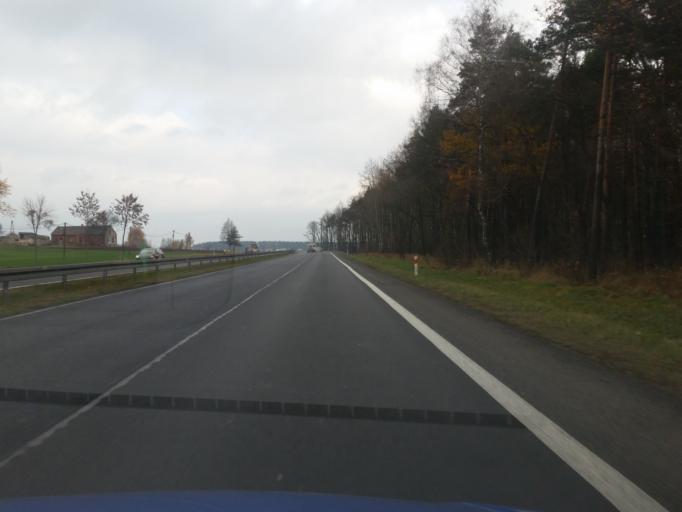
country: PL
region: Silesian Voivodeship
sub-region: Powiat myszkowski
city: Kozieglowy
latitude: 50.5447
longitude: 19.1808
